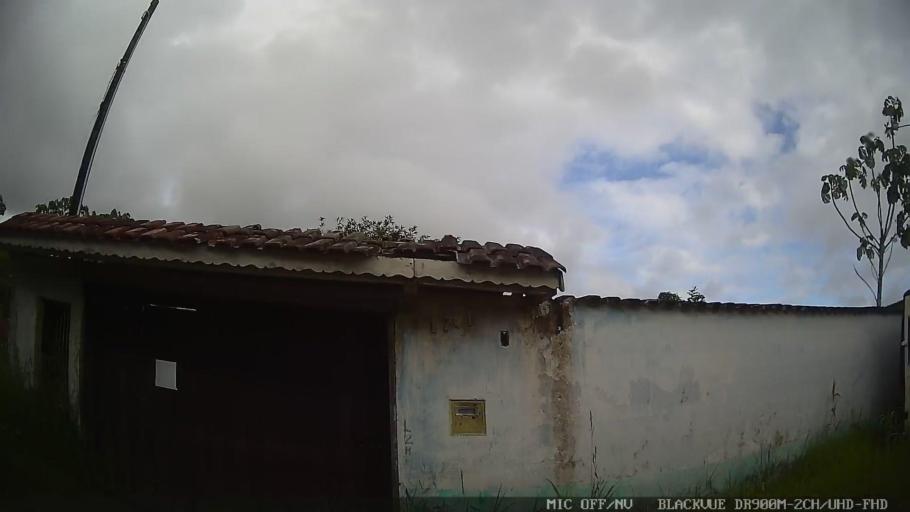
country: BR
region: Sao Paulo
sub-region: Itanhaem
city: Itanhaem
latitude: -24.2167
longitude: -46.8819
